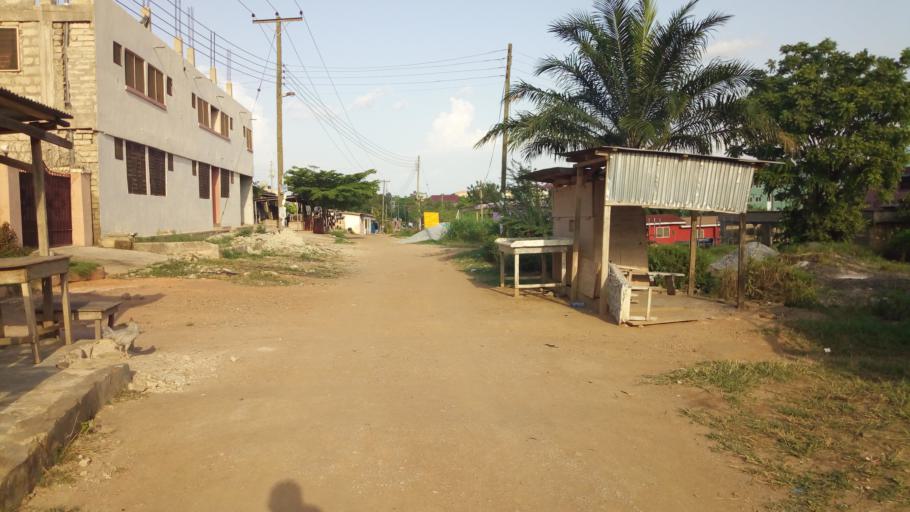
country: GH
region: Ashanti
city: Mamponteng
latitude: 6.6737
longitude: -1.5629
